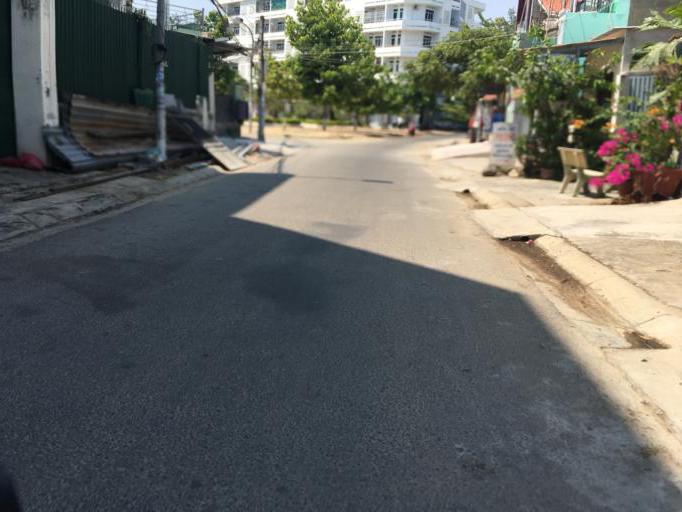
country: VN
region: Ninh Thuan
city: Phan Rang-Thap Cham
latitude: 11.5686
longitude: 108.9941
